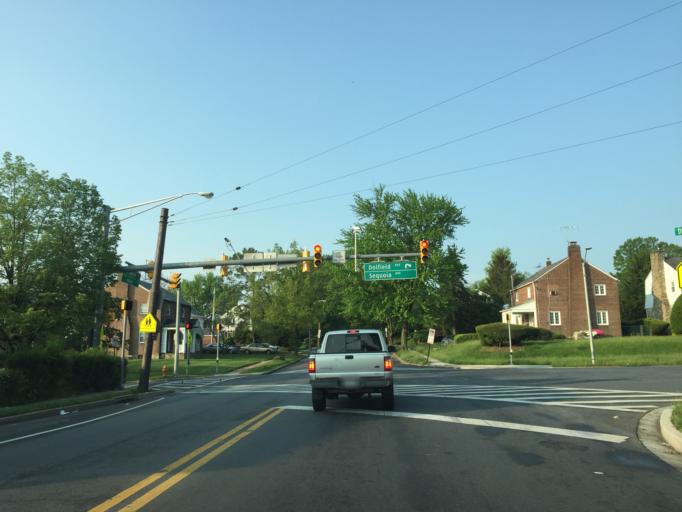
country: US
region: Maryland
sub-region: Baltimore County
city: Lochearn
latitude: 39.3293
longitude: -76.6690
